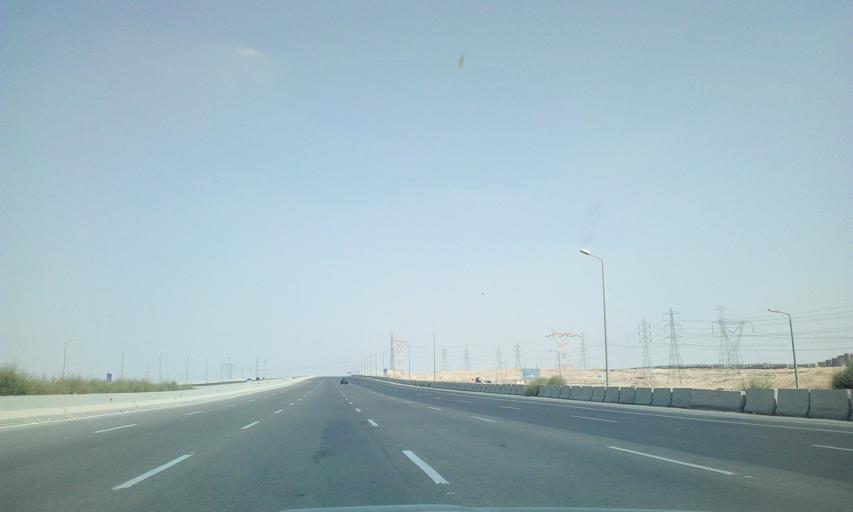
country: EG
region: Muhafazat al Qahirah
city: Halwan
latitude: 29.9065
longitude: 31.6736
